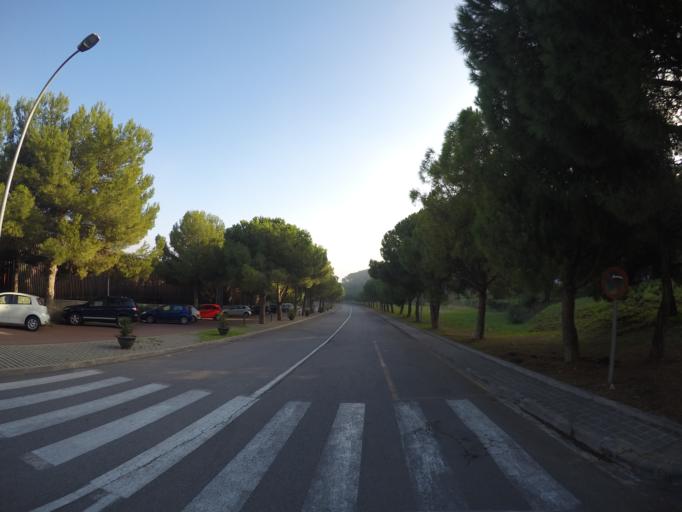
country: ES
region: Catalonia
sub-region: Provincia de Barcelona
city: Castelldefels
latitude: 41.2652
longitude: 1.9268
